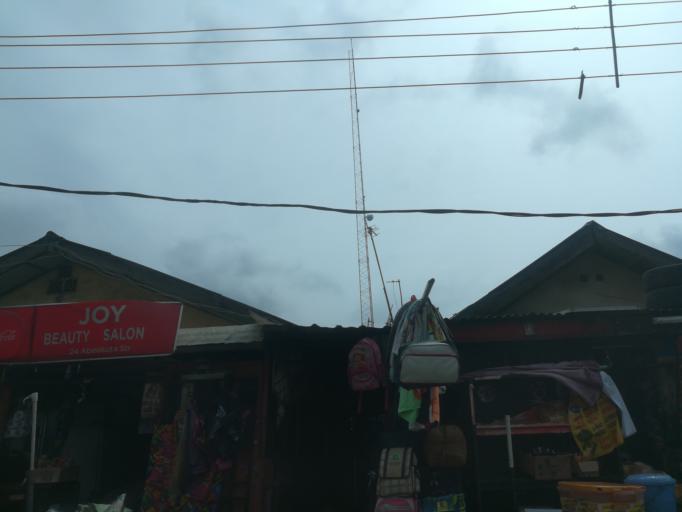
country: NG
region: Lagos
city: Ikeja
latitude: 6.6002
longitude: 3.3384
